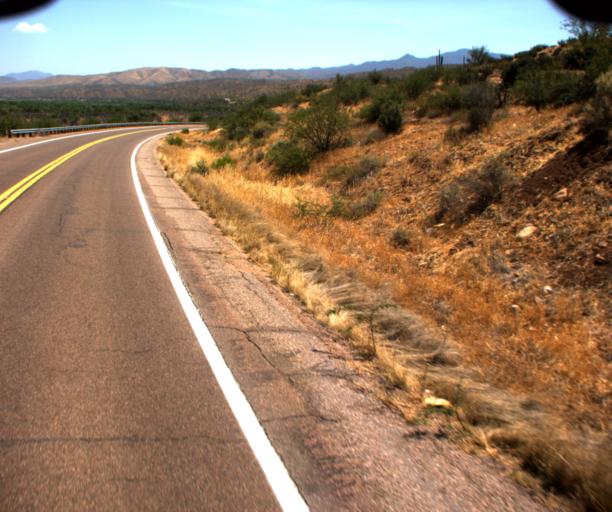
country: US
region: Arizona
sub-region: Gila County
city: Tonto Basin
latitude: 33.7867
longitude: -111.2640
